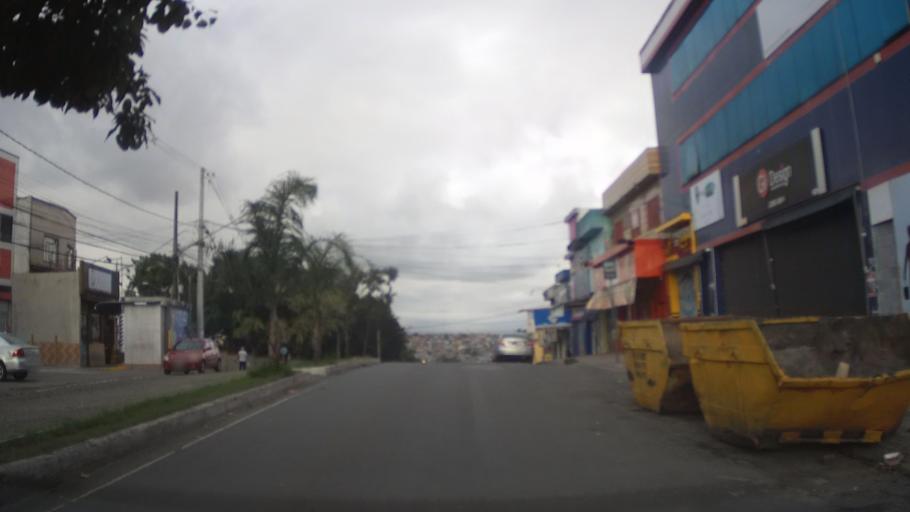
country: BR
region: Sao Paulo
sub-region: Itaquaquecetuba
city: Itaquaquecetuba
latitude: -23.4452
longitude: -46.4136
